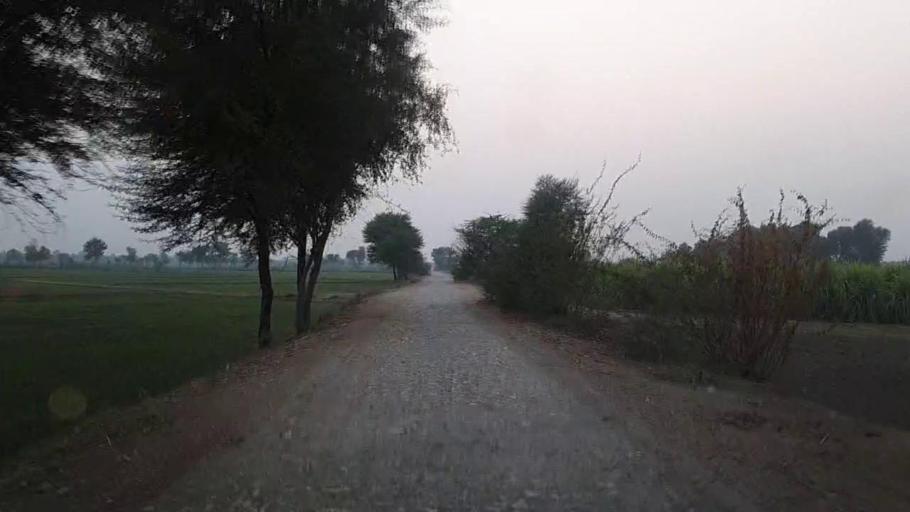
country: PK
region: Sindh
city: Kandiari
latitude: 26.9732
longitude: 68.4768
